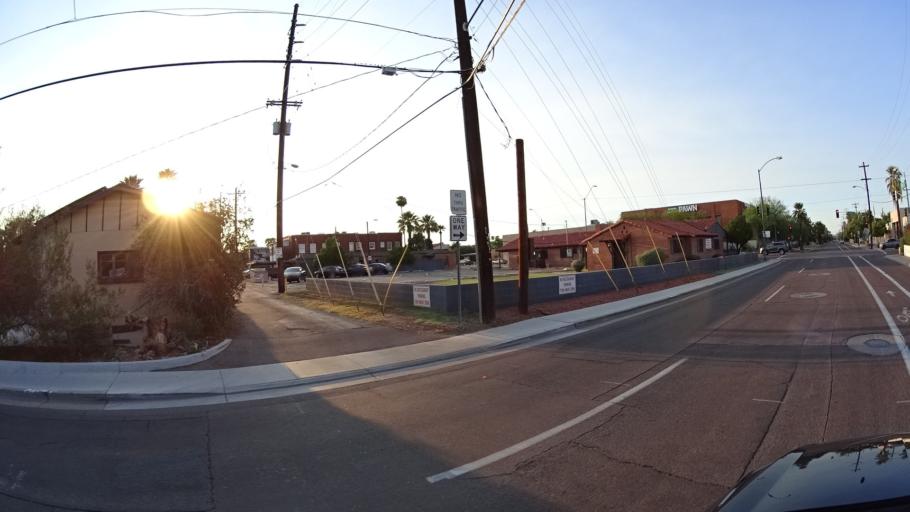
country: US
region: Arizona
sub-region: Maricopa County
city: Phoenix
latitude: 33.4652
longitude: -112.0783
